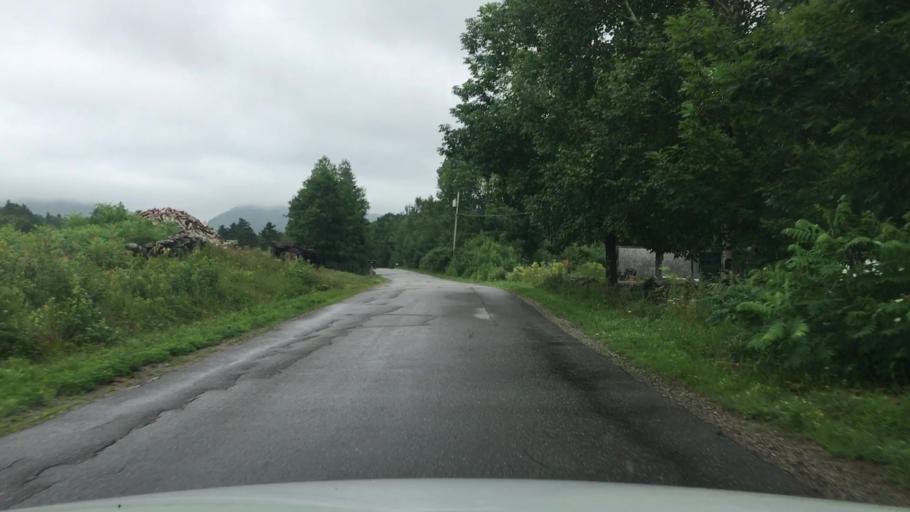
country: US
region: Maine
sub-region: Knox County
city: Hope
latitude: 44.2272
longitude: -69.1775
